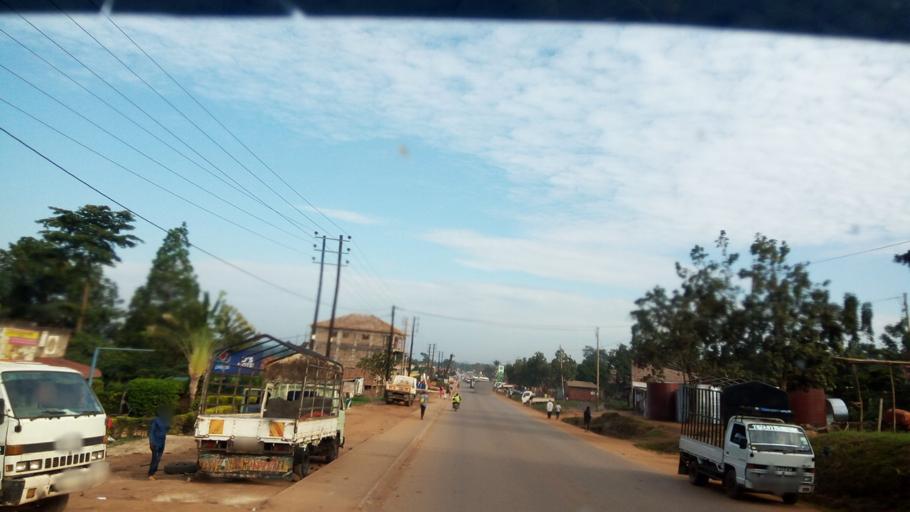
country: UG
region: Central Region
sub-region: Wakiso District
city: Wakiso
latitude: 0.4620
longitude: 32.5262
